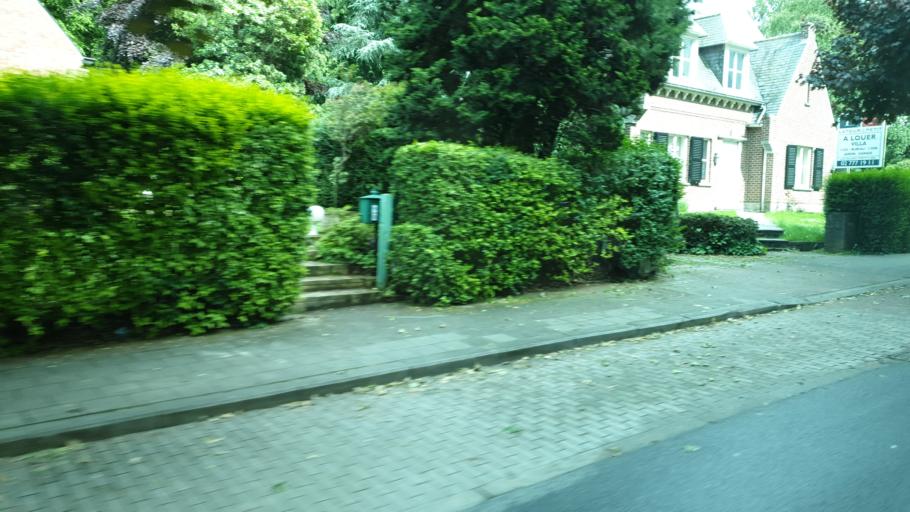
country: BE
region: Flanders
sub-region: Provincie Vlaams-Brabant
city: Wezembeek-Oppem
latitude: 50.8282
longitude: 4.4664
